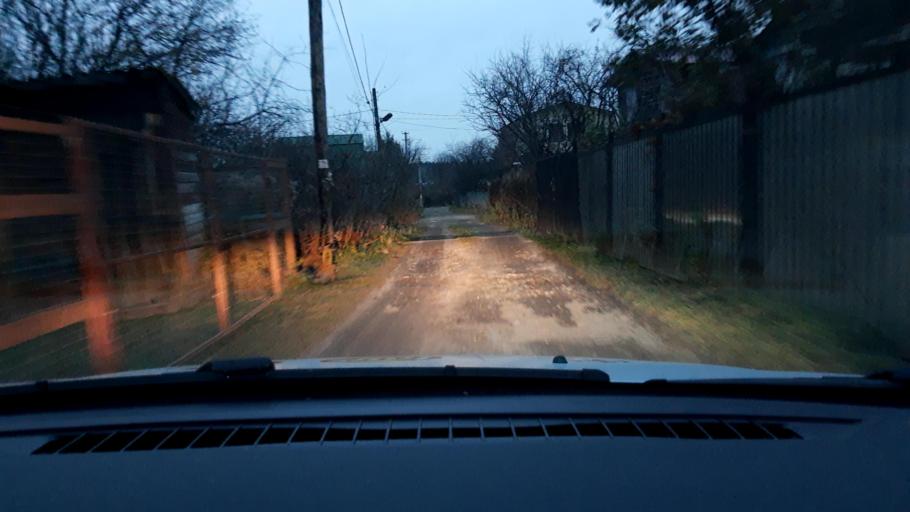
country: RU
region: Nizjnij Novgorod
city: Neklyudovo
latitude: 56.4297
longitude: 44.0092
